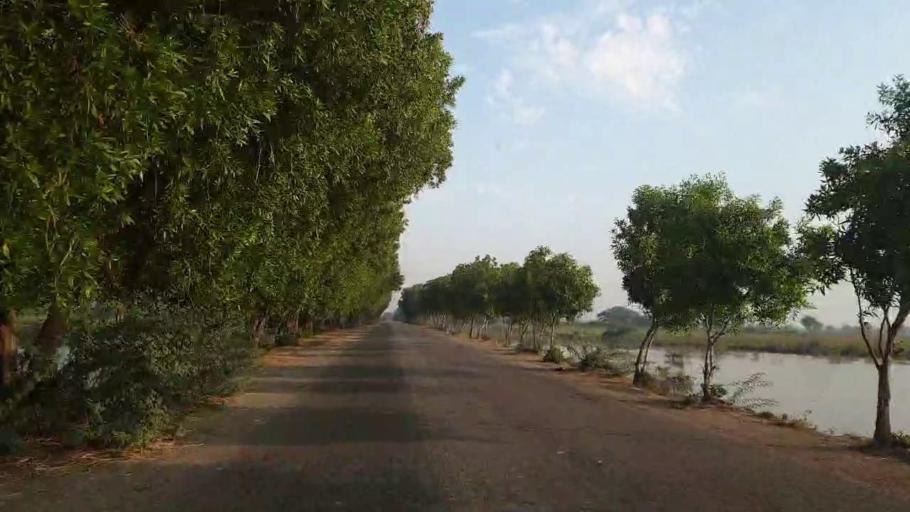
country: PK
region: Sindh
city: Tando Bago
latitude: 24.7501
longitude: 68.9498
